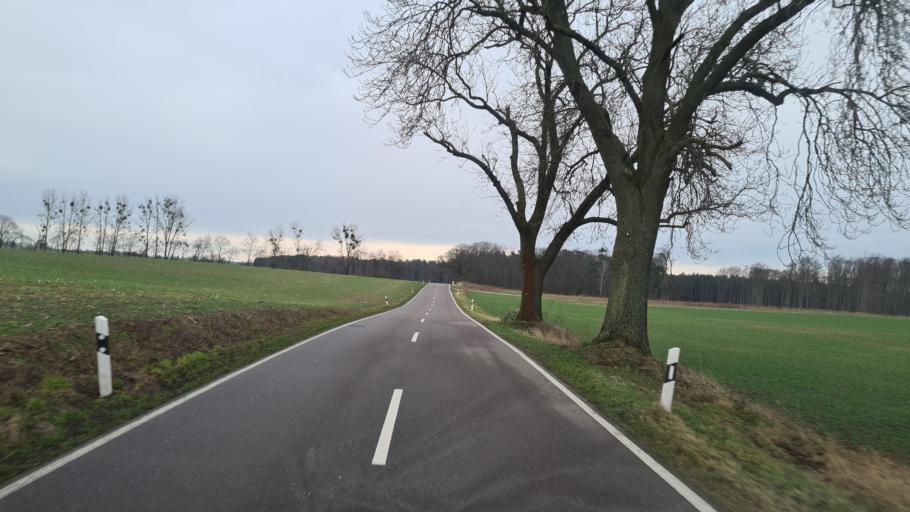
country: DE
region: Brandenburg
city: Gransee
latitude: 52.9399
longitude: 13.2271
